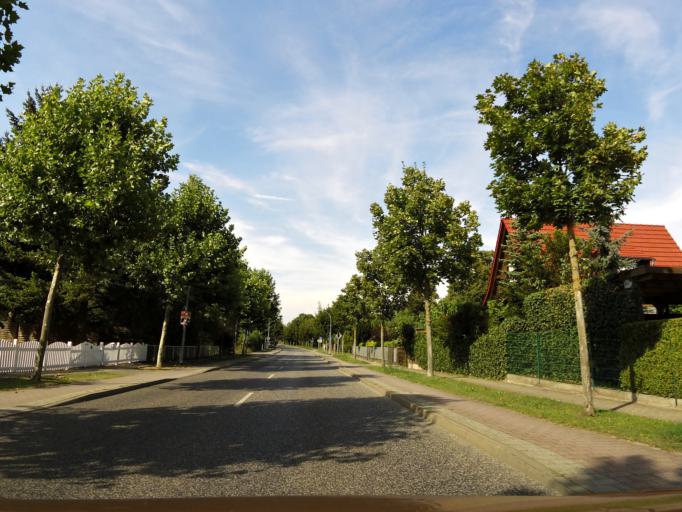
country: DE
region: Brandenburg
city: Teltow
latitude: 52.3899
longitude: 13.2462
